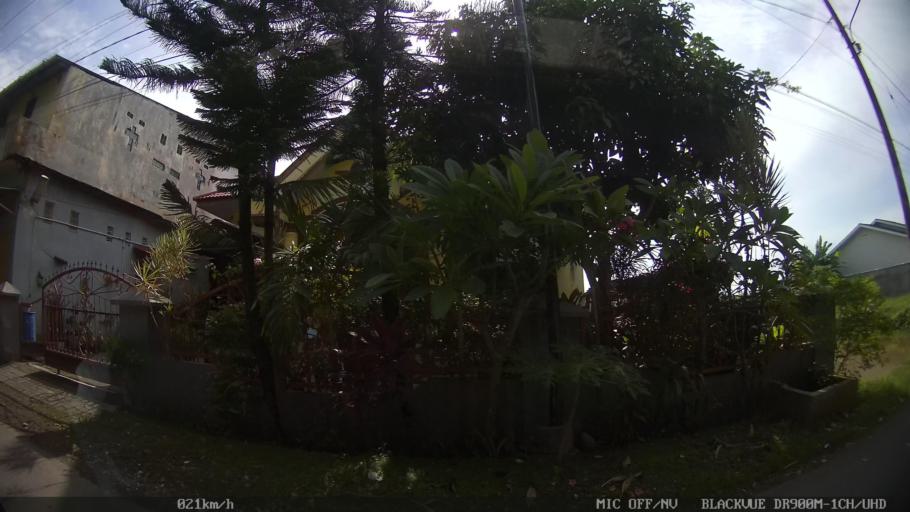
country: ID
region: North Sumatra
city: Medan
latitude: 3.6202
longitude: 98.6603
